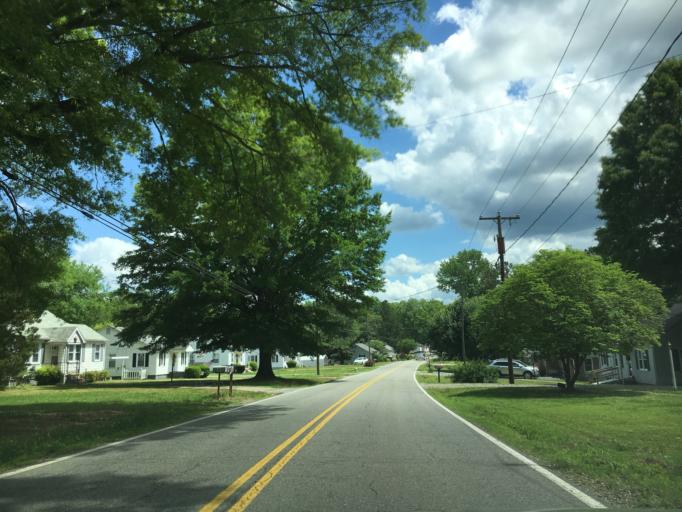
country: US
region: Virginia
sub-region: Halifax County
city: South Boston
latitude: 36.7057
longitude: -78.9271
